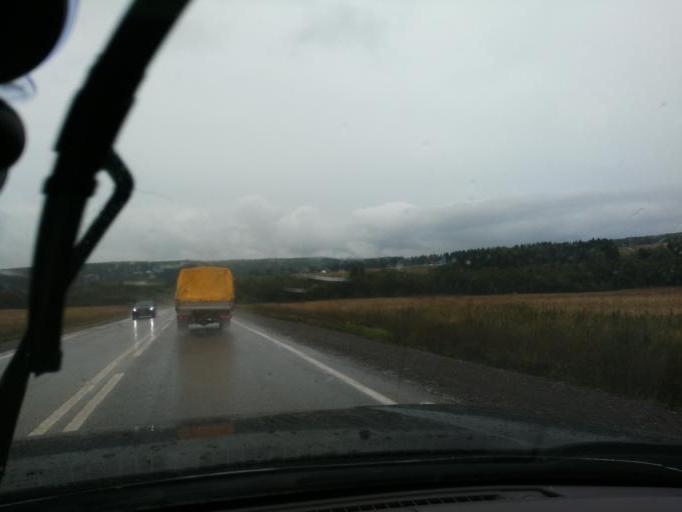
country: RU
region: Perm
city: Yugo-Kamskiy
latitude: 57.7088
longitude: 55.6329
